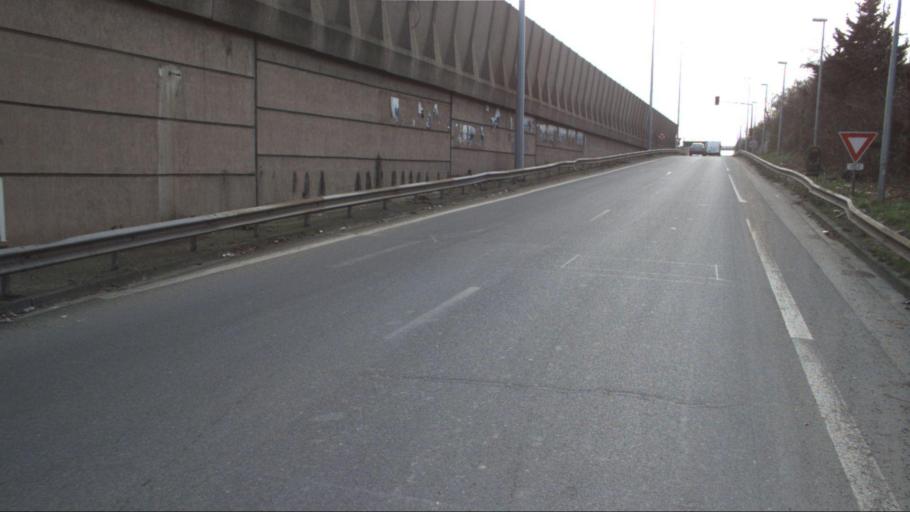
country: FR
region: Ile-de-France
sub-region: Departement du Val-de-Marne
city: Fontenay-sous-Bois
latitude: 48.8521
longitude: 2.4894
